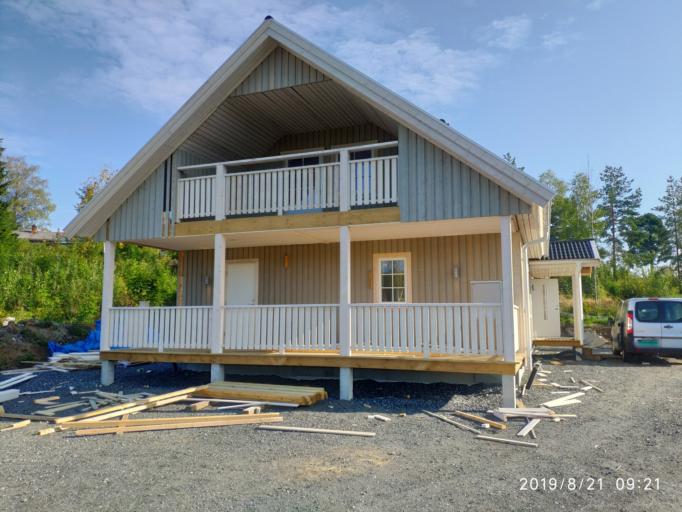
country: NO
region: Buskerud
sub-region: Kongsberg
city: Kongsberg
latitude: 59.6992
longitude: 9.7865
